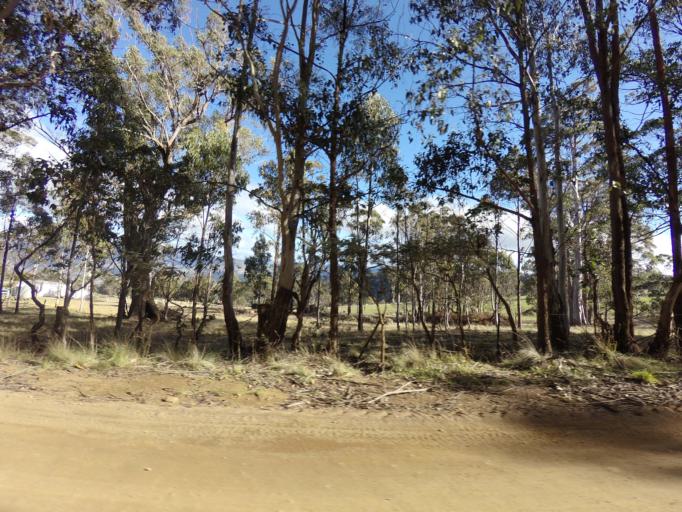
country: AU
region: Tasmania
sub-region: Derwent Valley
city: New Norfolk
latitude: -42.7154
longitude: 147.0319
